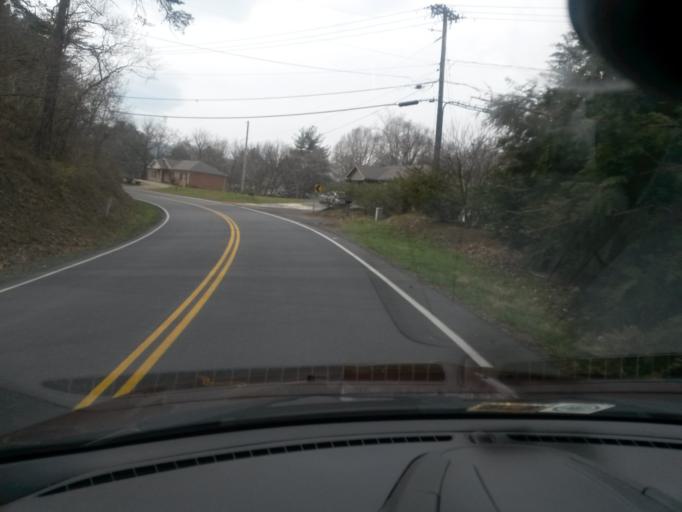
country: US
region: Virginia
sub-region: Roanoke County
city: Cave Spring
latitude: 37.2454
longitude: -80.0078
